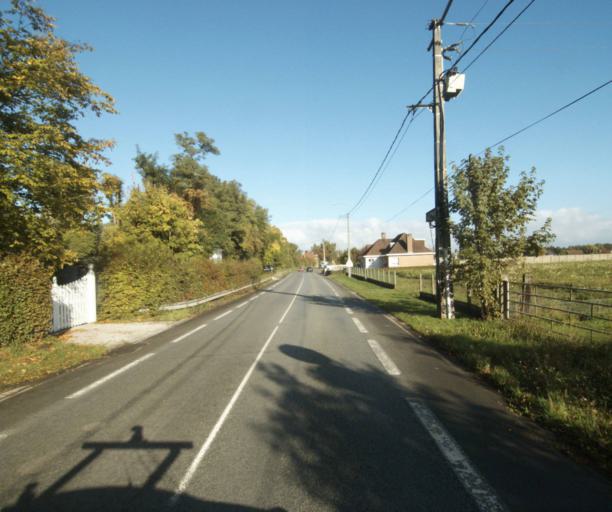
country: FR
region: Nord-Pas-de-Calais
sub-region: Departement du Nord
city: Verlinghem
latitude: 50.6724
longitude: 3.0031
